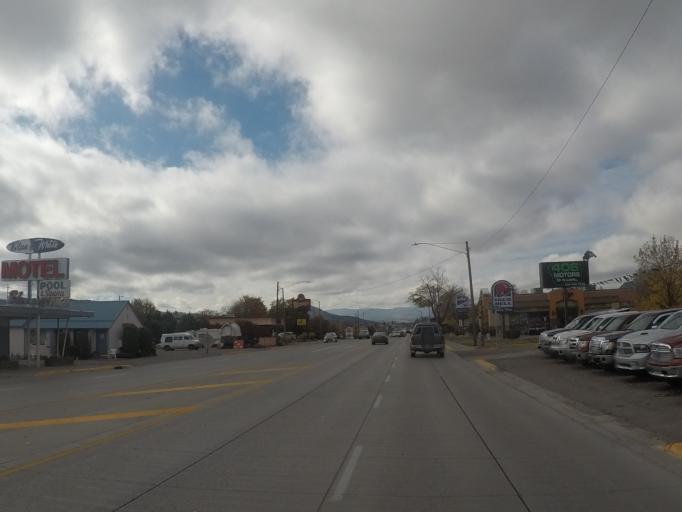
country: US
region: Montana
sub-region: Flathead County
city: Kalispell
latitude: 48.2040
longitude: -114.3040
